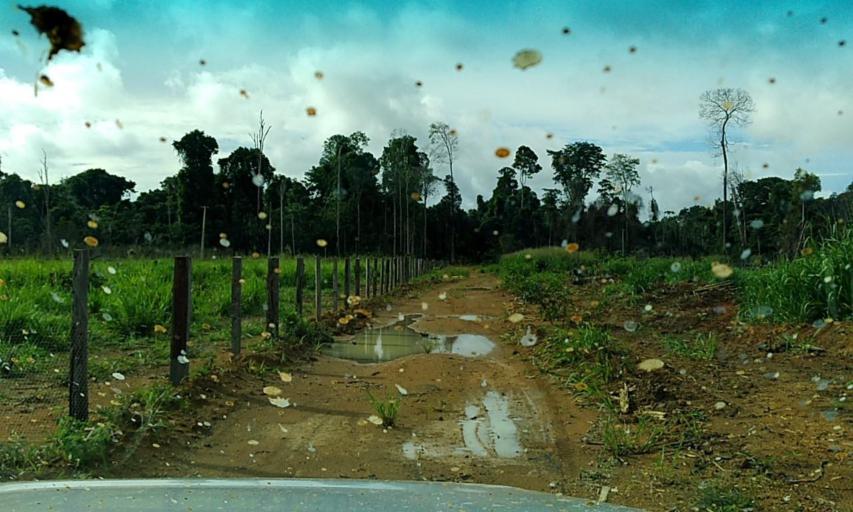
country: BR
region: Para
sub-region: Senador Jose Porfirio
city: Senador Jose Porfirio
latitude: -2.9990
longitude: -51.7415
